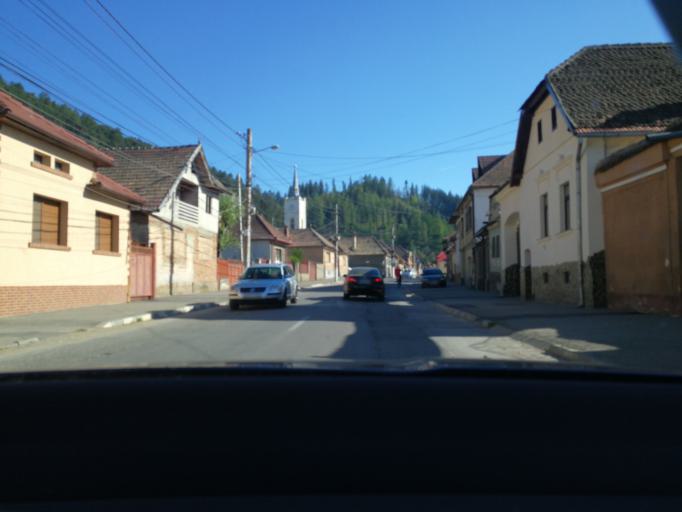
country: RO
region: Brasov
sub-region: Oras Rasnov
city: Rasnov
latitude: 45.5848
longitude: 25.4615
